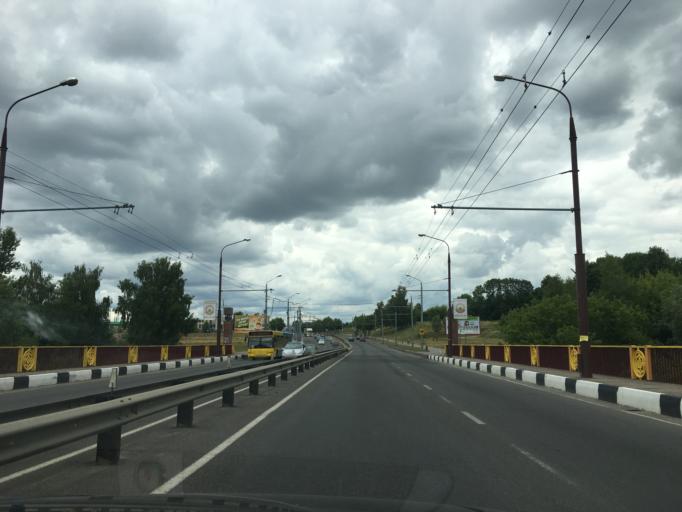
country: BY
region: Grodnenskaya
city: Hrodna
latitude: 53.6618
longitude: 23.8599
